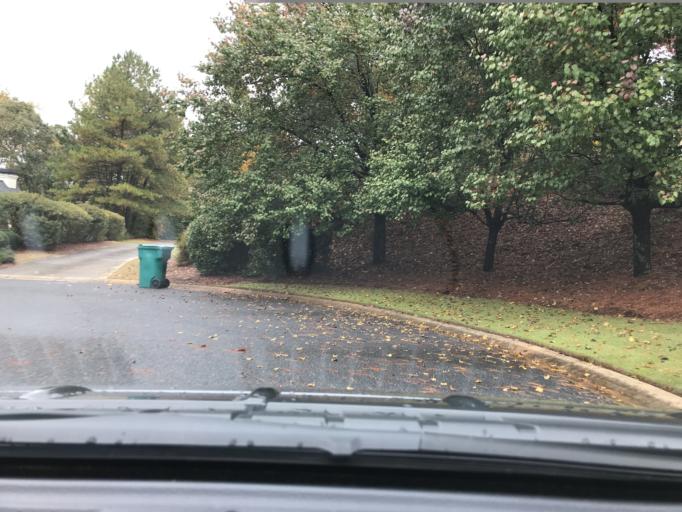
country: US
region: Georgia
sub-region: Fulton County
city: Johns Creek
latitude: 34.0138
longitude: -84.2505
